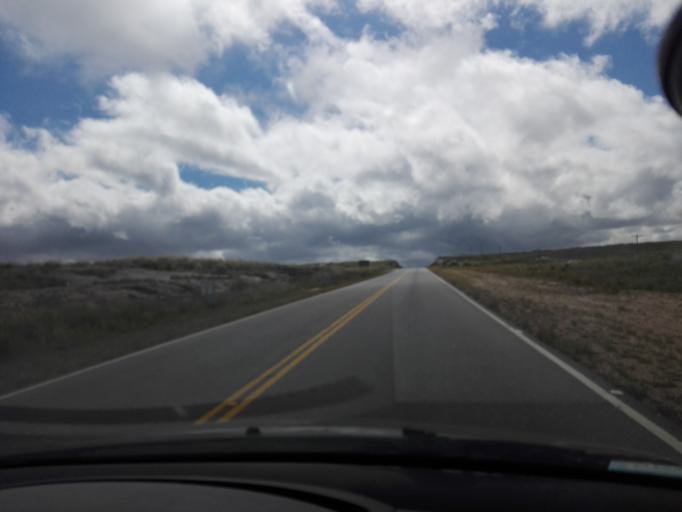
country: AR
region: Cordoba
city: Mina Clavero
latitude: -31.6110
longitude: -64.8238
